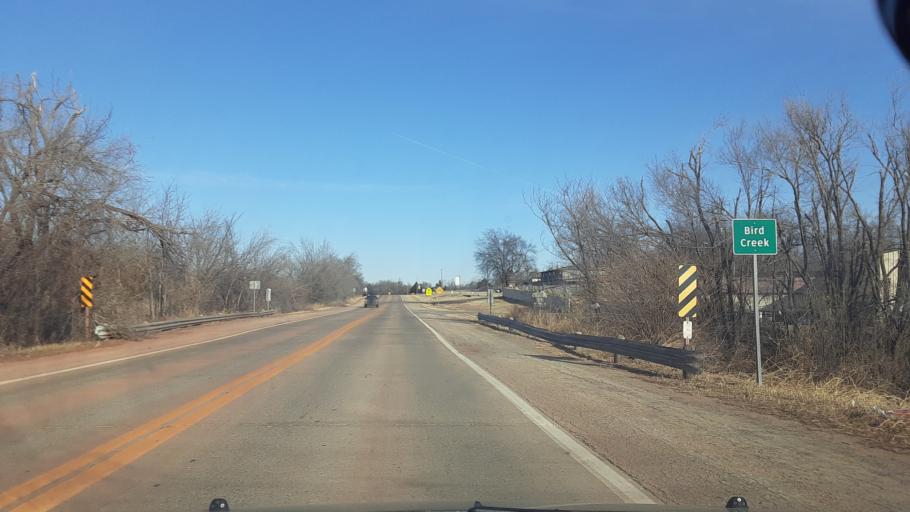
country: US
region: Oklahoma
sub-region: Logan County
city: Guthrie
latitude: 35.8895
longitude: -97.4240
